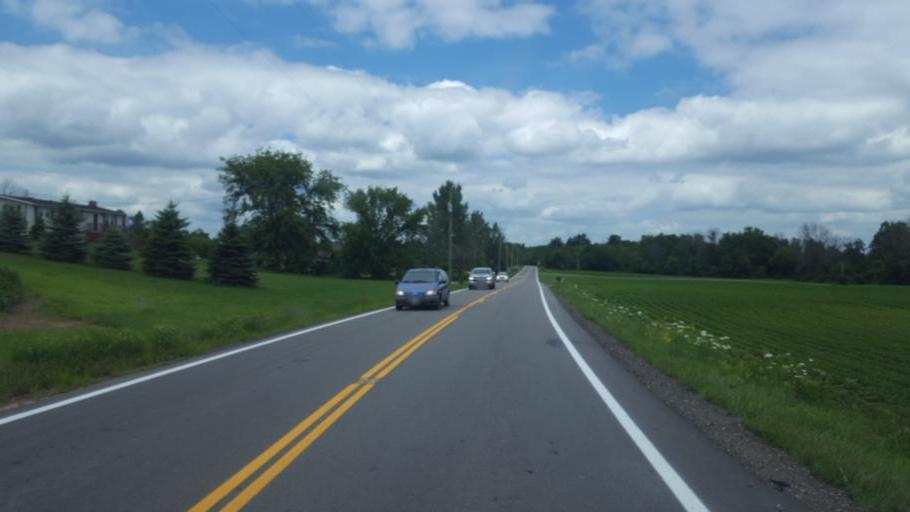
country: US
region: Ohio
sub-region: Richland County
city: Ontario
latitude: 40.8028
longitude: -82.6559
